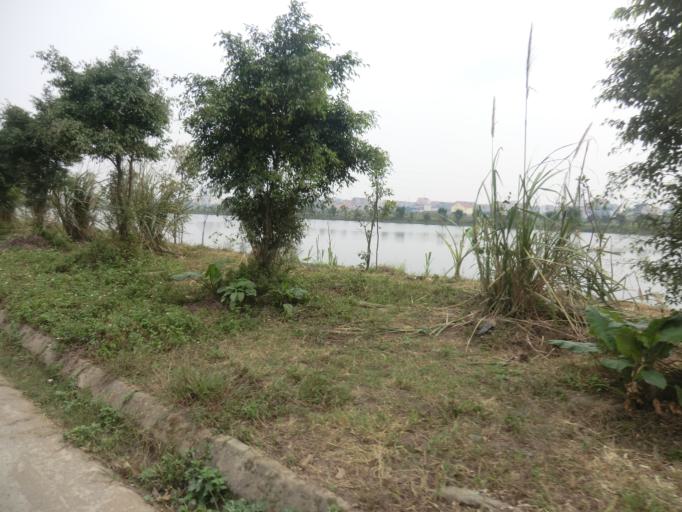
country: VN
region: Ninh Binh
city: Thanh Pho Ninh Binh
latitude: 20.2608
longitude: 105.9571
